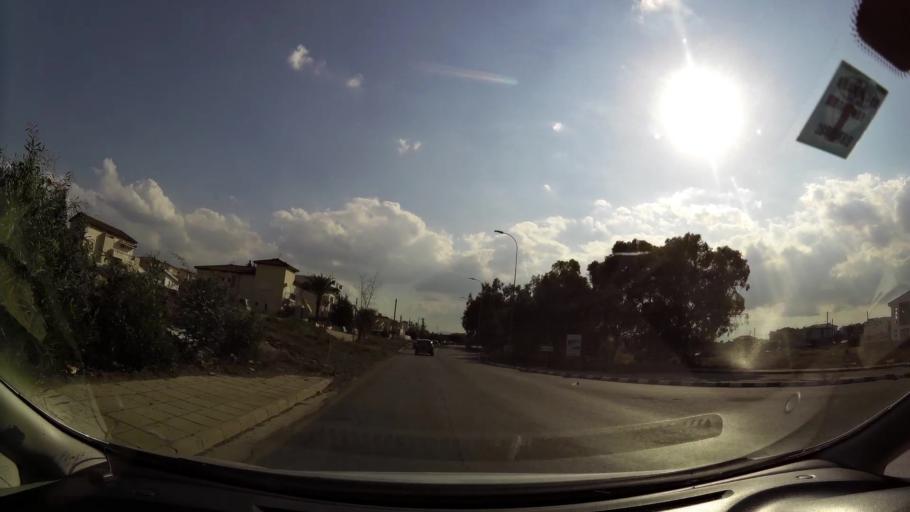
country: CY
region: Lefkosia
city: Kato Deftera
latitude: 35.1340
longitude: 33.3002
